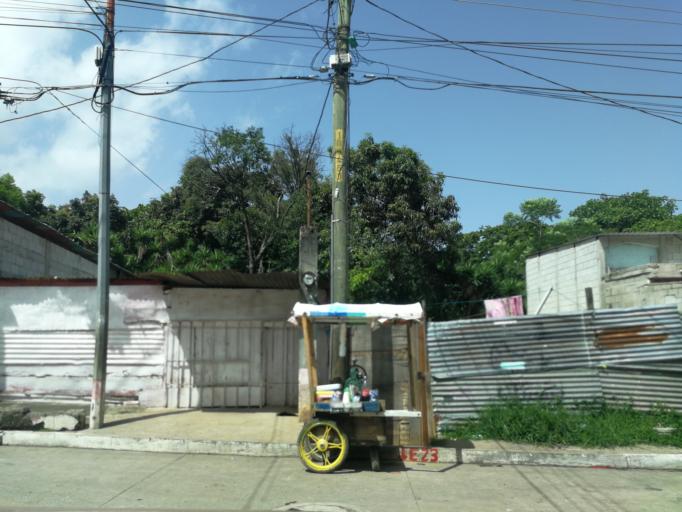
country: GT
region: Guatemala
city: Santa Catarina Pinula
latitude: 14.5450
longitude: -90.5174
